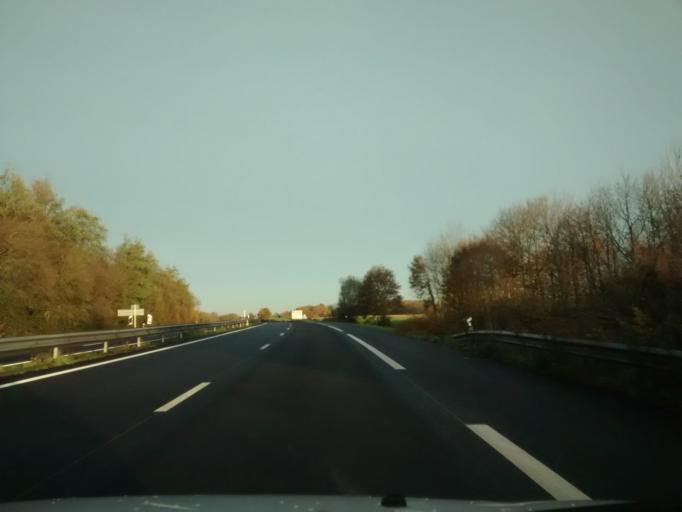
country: FR
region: Brittany
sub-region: Departement d'Ille-et-Vilaine
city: Hede-Bazouges
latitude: 48.2894
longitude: -1.8037
